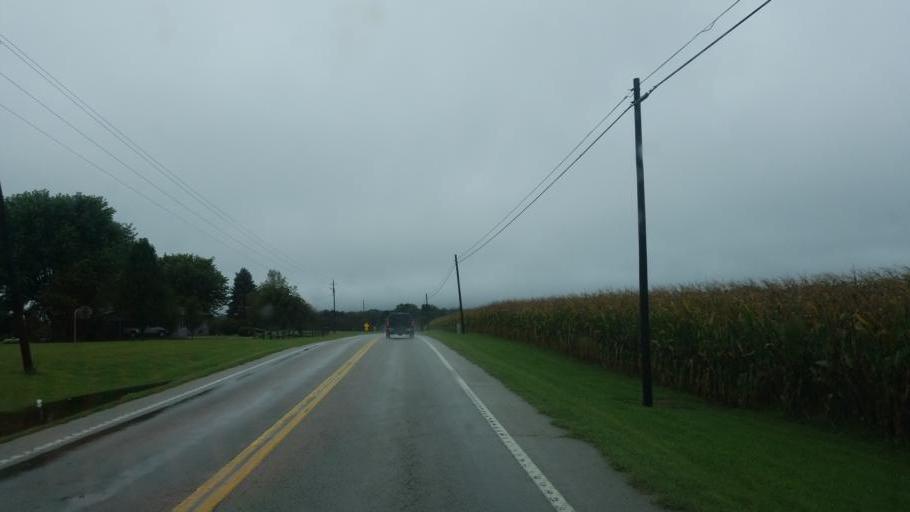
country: US
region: Ohio
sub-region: Adams County
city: West Union
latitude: 38.7978
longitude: -83.4992
